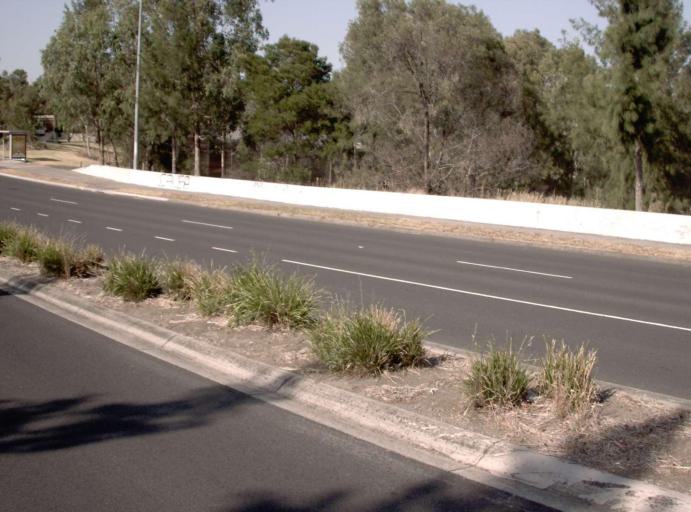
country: AU
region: Victoria
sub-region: Whitehorse
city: Box Hill North
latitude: -37.7980
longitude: 145.1271
